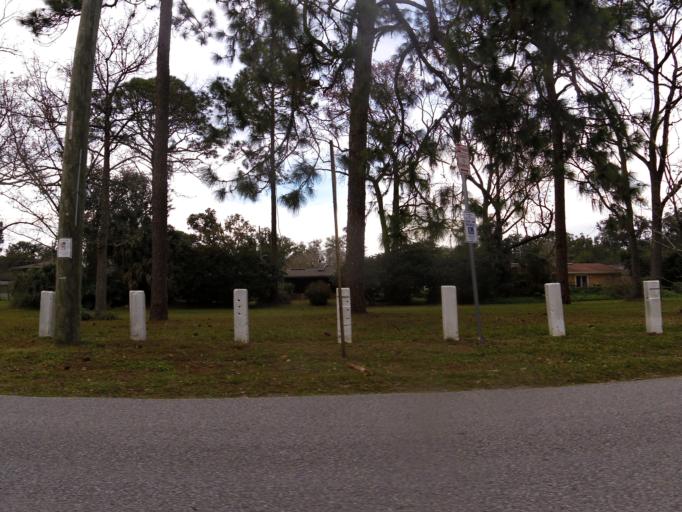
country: US
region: Florida
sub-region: Duval County
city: Jacksonville
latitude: 30.2470
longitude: -81.6274
